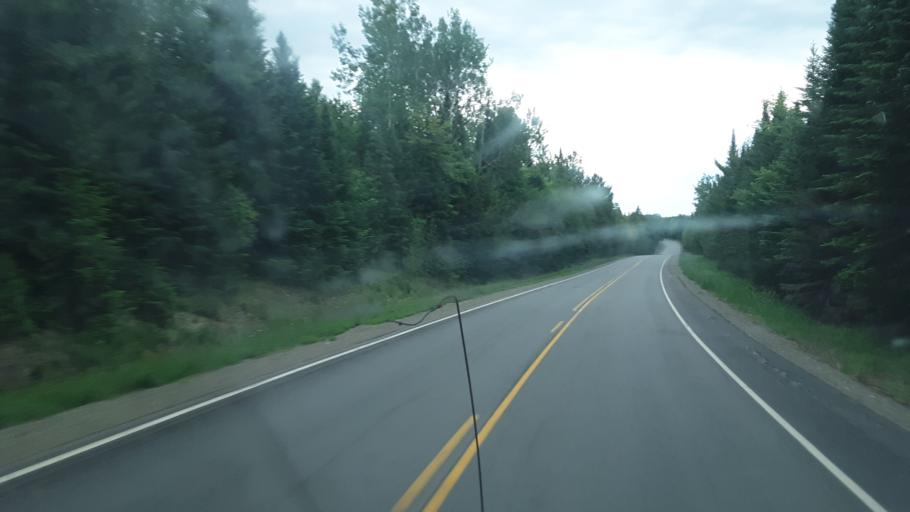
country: US
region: Maine
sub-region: Penobscot County
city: Medway
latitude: 45.7428
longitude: -68.3079
